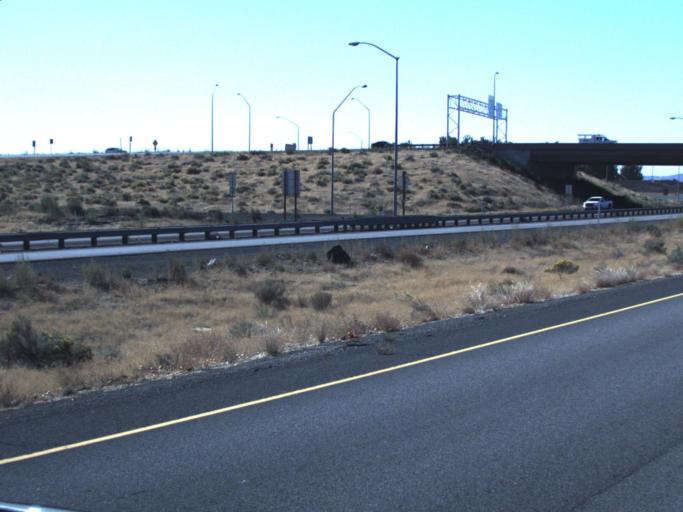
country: US
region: Washington
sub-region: Franklin County
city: Pasco
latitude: 46.2519
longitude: -119.0810
